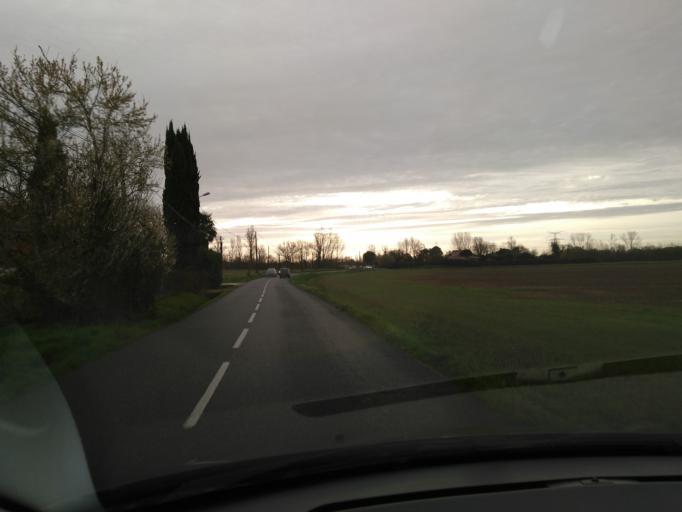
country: FR
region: Midi-Pyrenees
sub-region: Departement de la Haute-Garonne
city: Cepet
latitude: 43.7570
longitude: 1.4395
